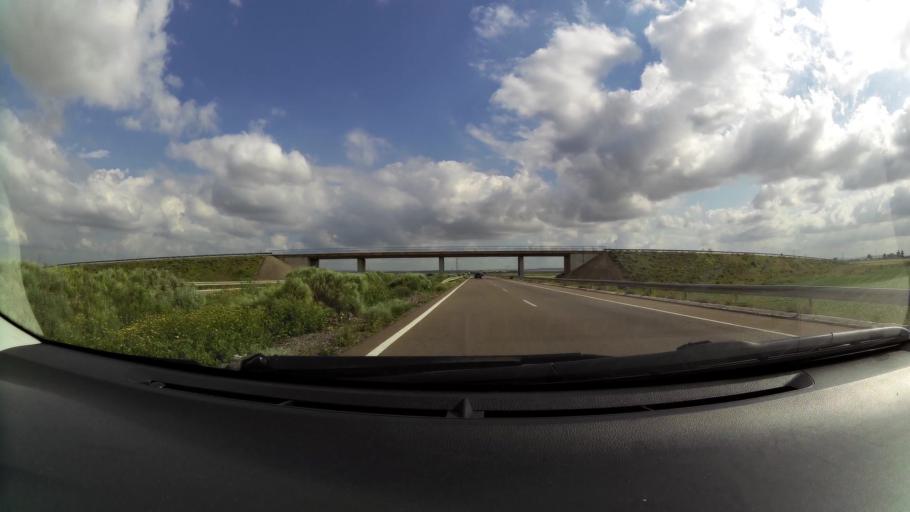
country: MA
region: Chaouia-Ouardigha
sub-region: Settat Province
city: Berrechid
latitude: 33.1787
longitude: -7.5726
